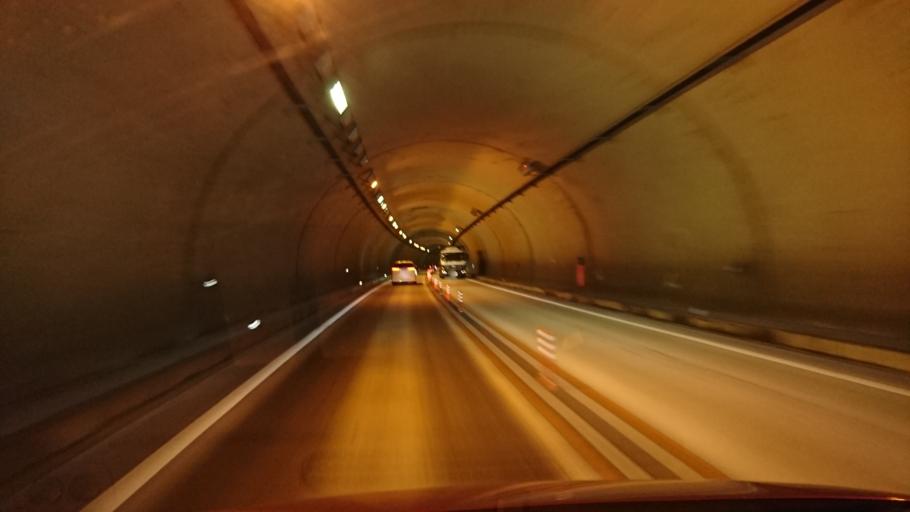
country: JP
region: Hiroshima
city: Innoshima
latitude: 34.2962
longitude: 133.1447
